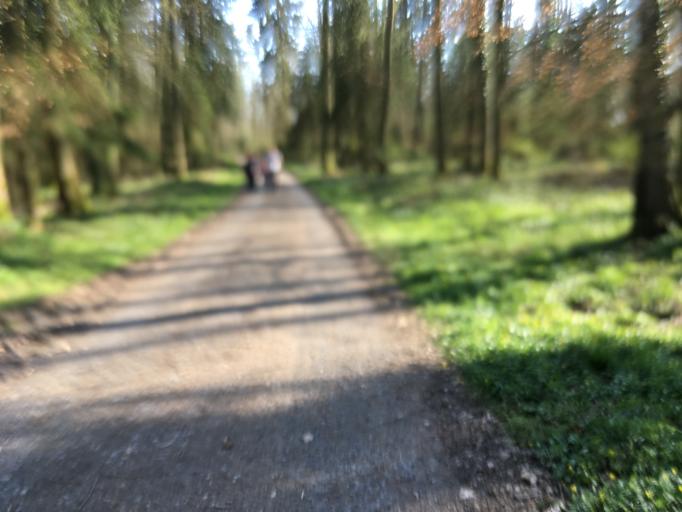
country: DE
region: Baden-Wuerttemberg
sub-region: Regierungsbezirk Stuttgart
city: Leingarten
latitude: 49.1696
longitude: 9.0873
